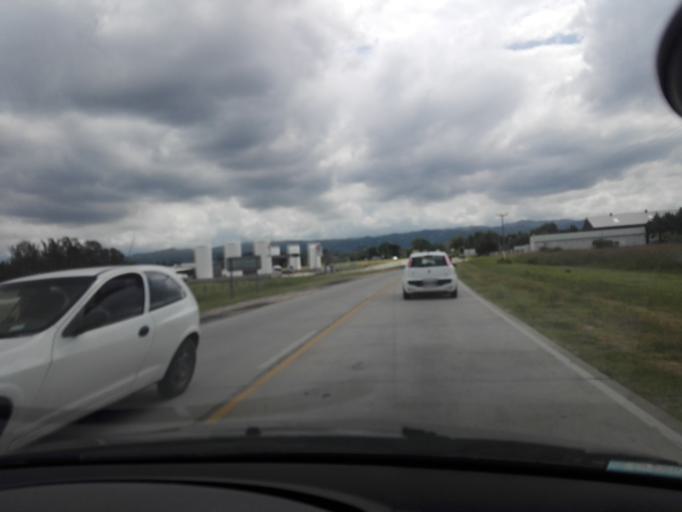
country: AR
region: Cordoba
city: Alta Gracia
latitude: -31.6347
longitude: -64.4322
